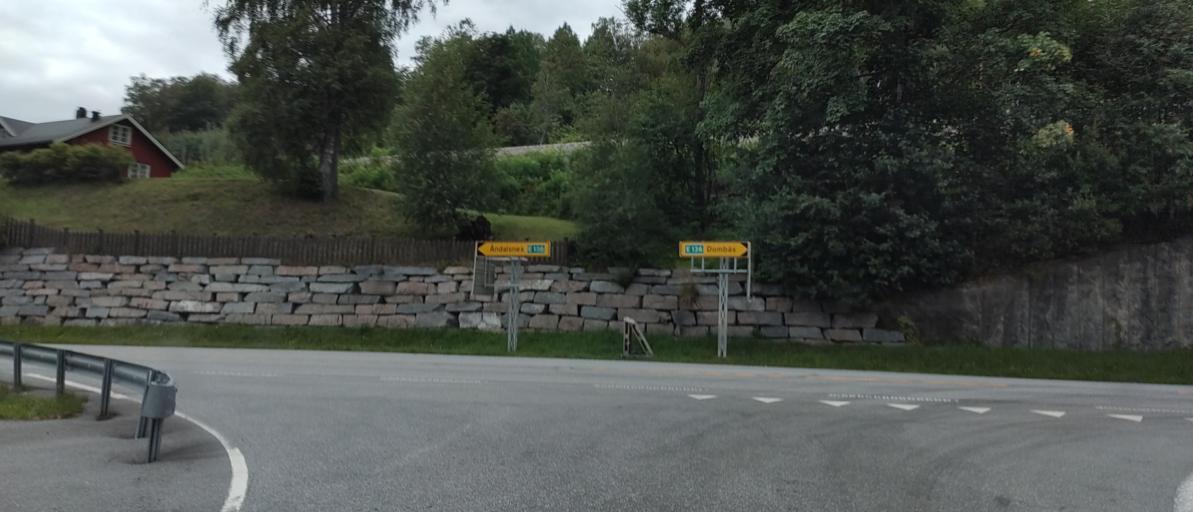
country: NO
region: More og Romsdal
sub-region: Rauma
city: Andalsnes
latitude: 62.5329
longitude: 7.7367
